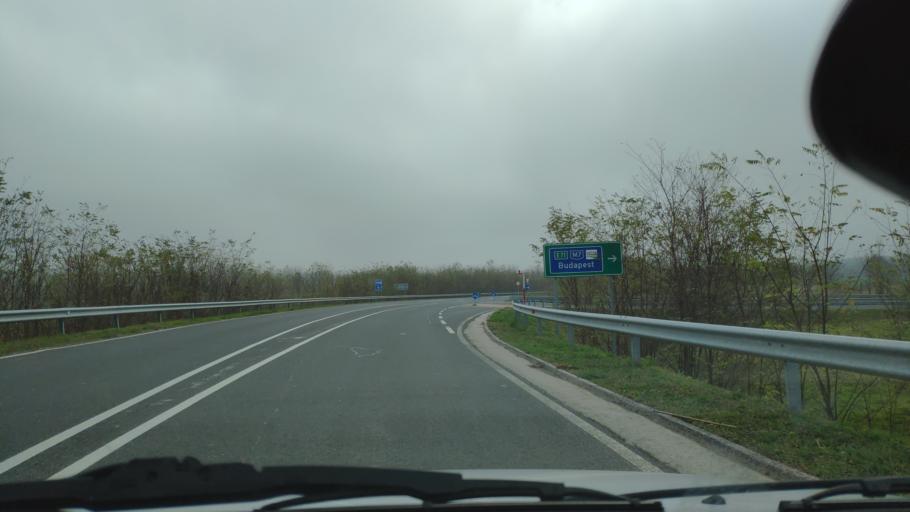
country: HU
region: Somogy
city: Balatonbereny
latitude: 46.6488
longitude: 17.3001
